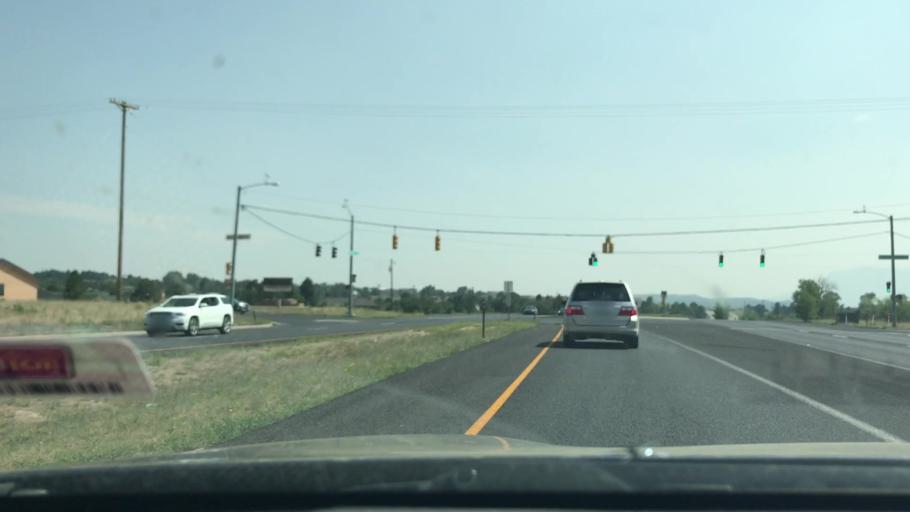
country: US
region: Colorado
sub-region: El Paso County
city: Air Force Academy
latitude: 38.9809
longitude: -104.7979
